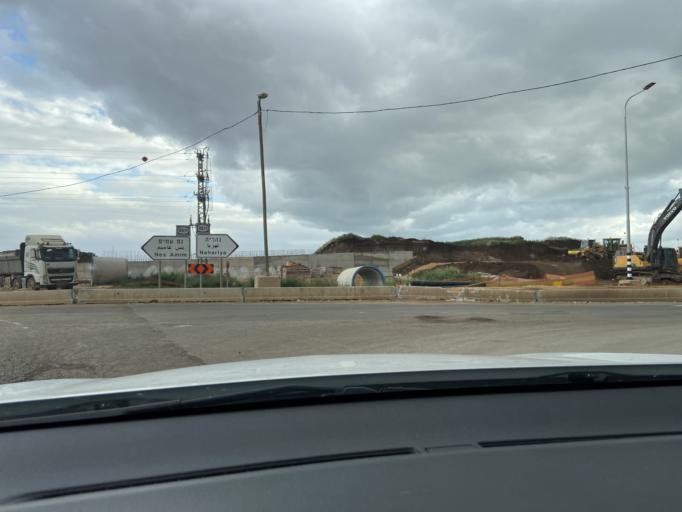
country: IL
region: Northern District
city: El Mazra`a
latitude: 32.9778
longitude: 35.1146
